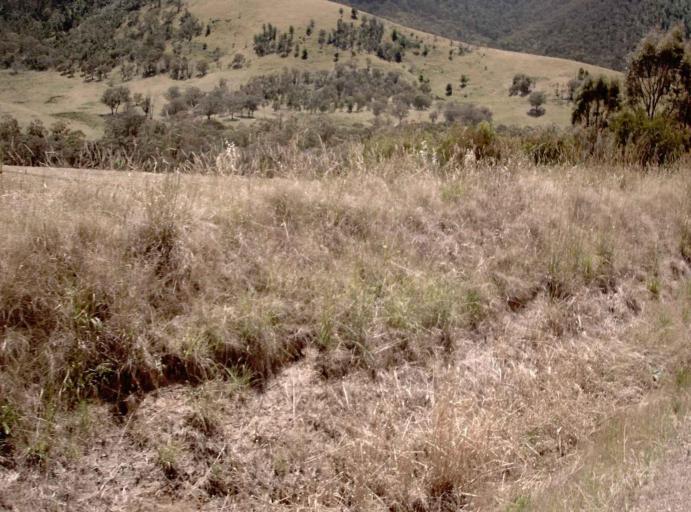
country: AU
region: Victoria
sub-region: East Gippsland
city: Bairnsdale
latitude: -37.1670
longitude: 147.6815
